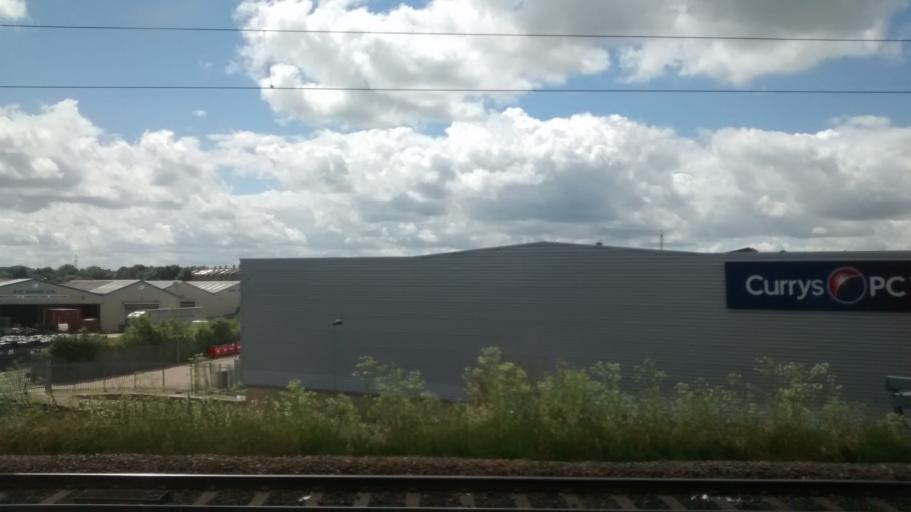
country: GB
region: England
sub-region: Lincolnshire
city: Grantham
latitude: 52.9102
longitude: -0.6468
